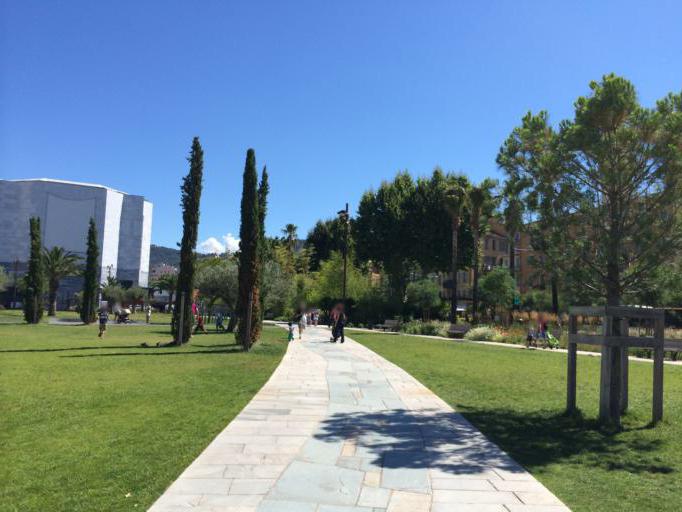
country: FR
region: Provence-Alpes-Cote d'Azur
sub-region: Departement des Alpes-Maritimes
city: Nice
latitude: 43.6993
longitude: 7.2768
